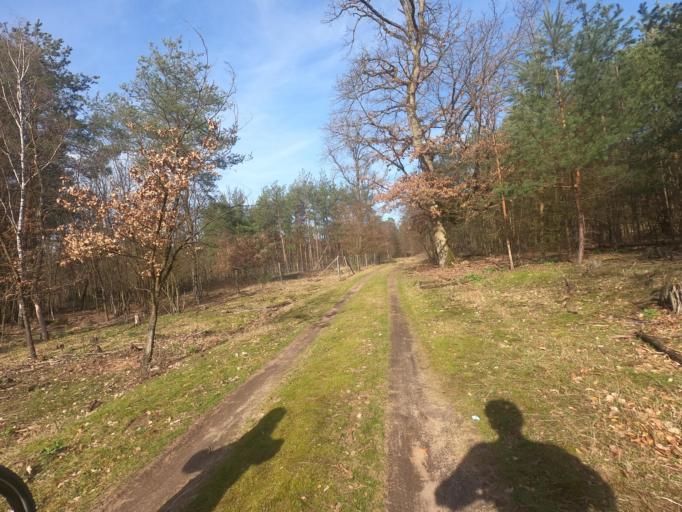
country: DE
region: Hesse
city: Raunheim
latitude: 49.9968
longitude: 8.5022
